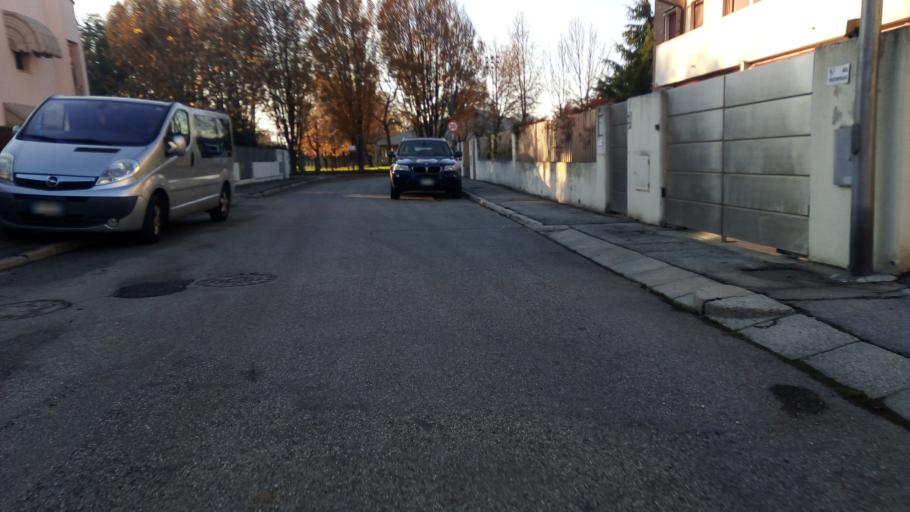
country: IT
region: Veneto
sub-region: Provincia di Padova
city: Abano Terme
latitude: 45.3632
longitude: 11.7857
